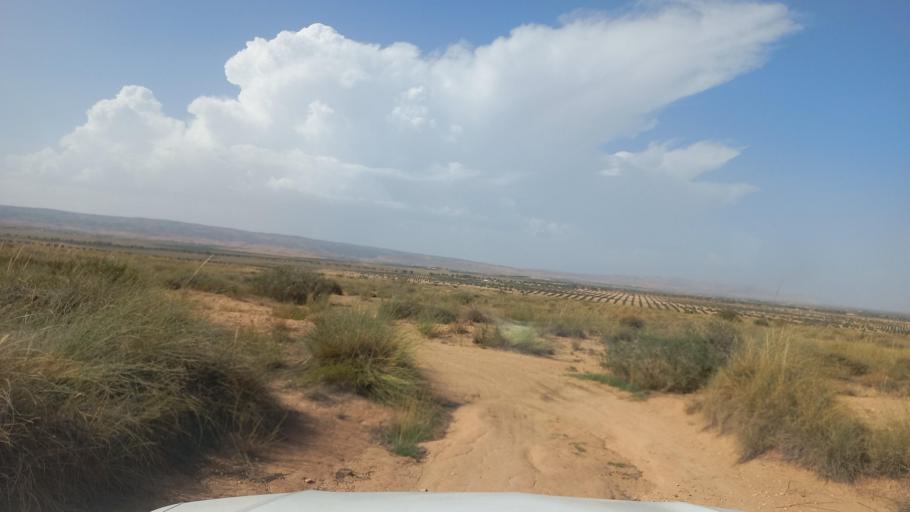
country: TN
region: Al Qasrayn
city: Kasserine
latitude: 35.2144
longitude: 8.9964
